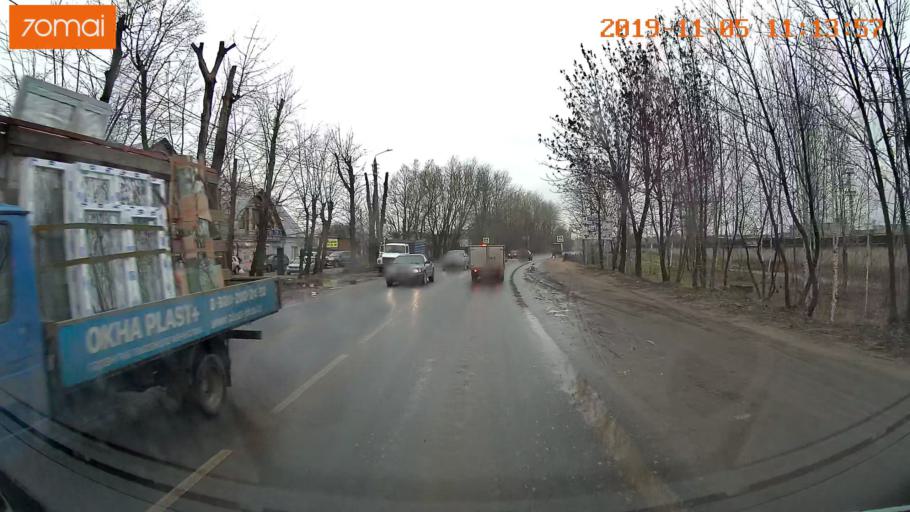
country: RU
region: Ivanovo
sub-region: Gorod Ivanovo
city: Ivanovo
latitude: 56.9678
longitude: 40.9523
